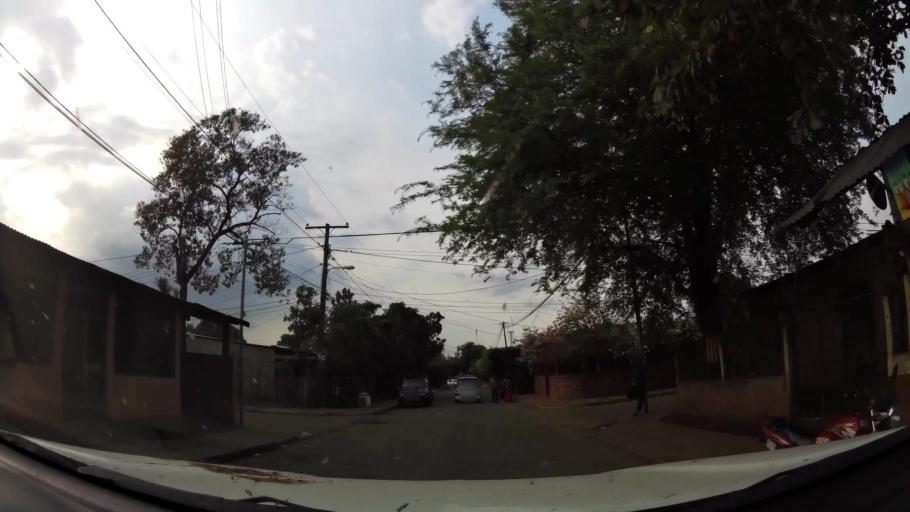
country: NI
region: Masaya
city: Masaya
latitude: 11.9818
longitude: -86.0993
